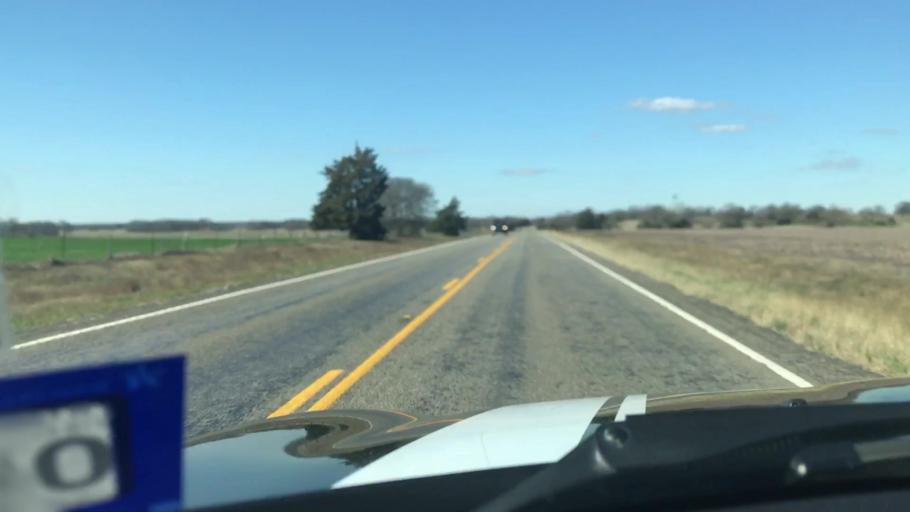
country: US
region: Texas
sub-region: Robertson County
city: Calvert
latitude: 30.8745
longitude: -96.7236
